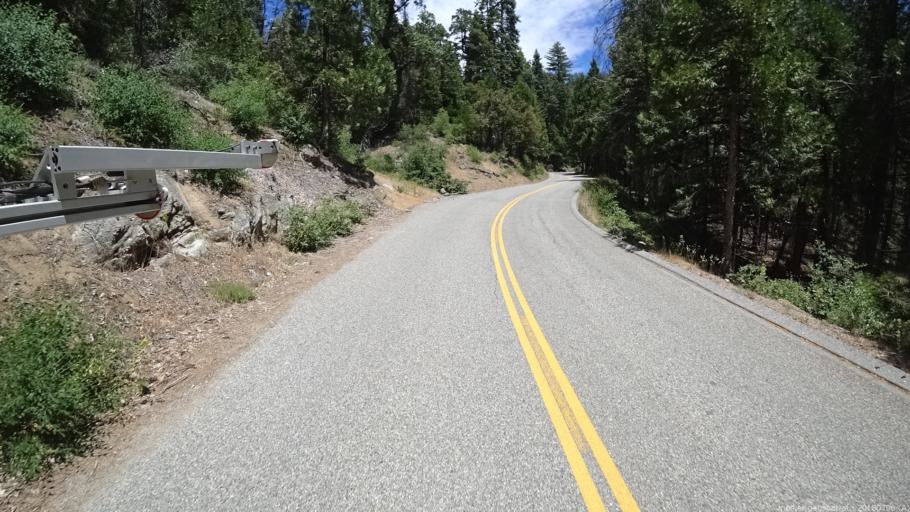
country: US
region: California
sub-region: Madera County
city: Oakhurst
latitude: 37.3766
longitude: -119.5282
